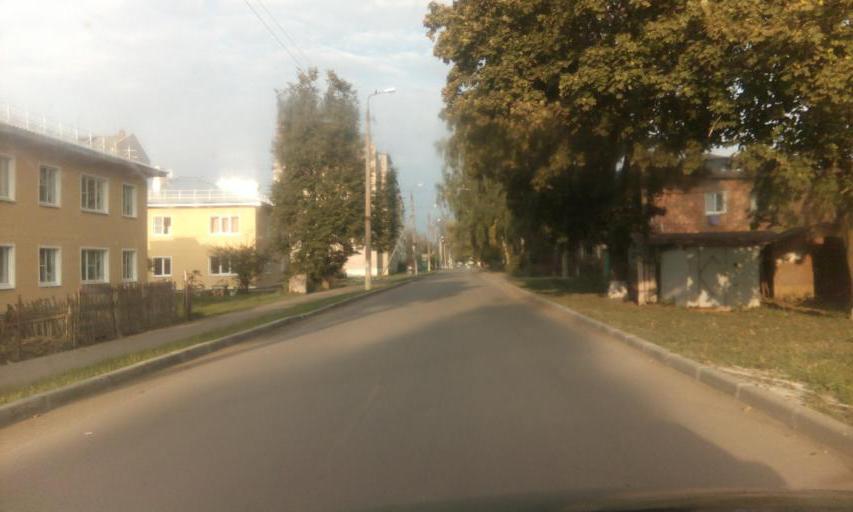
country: RU
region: Tula
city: Partizan
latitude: 53.9208
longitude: 38.0961
